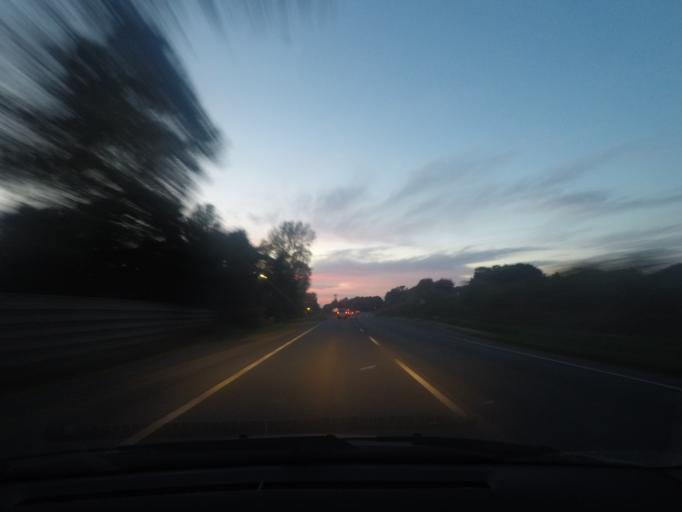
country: GB
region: England
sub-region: East Riding of Yorkshire
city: Wilberfoss
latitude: 53.9366
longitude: -0.8549
